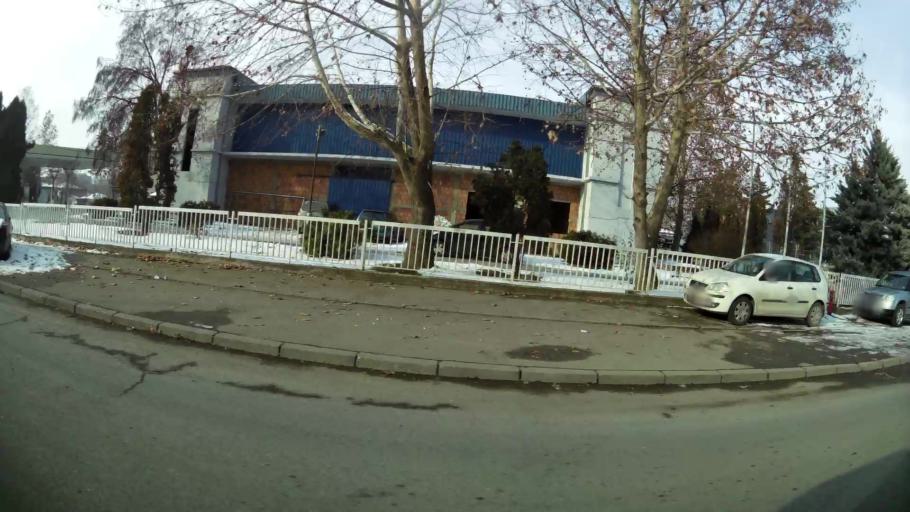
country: MK
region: Cair
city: Cair
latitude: 42.0242
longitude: 21.4341
